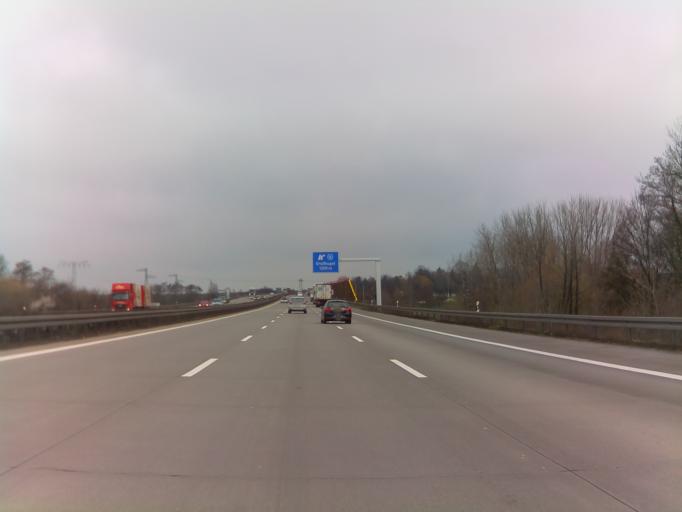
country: DE
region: Saxony-Anhalt
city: Ermlitz
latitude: 51.3855
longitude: 12.1828
